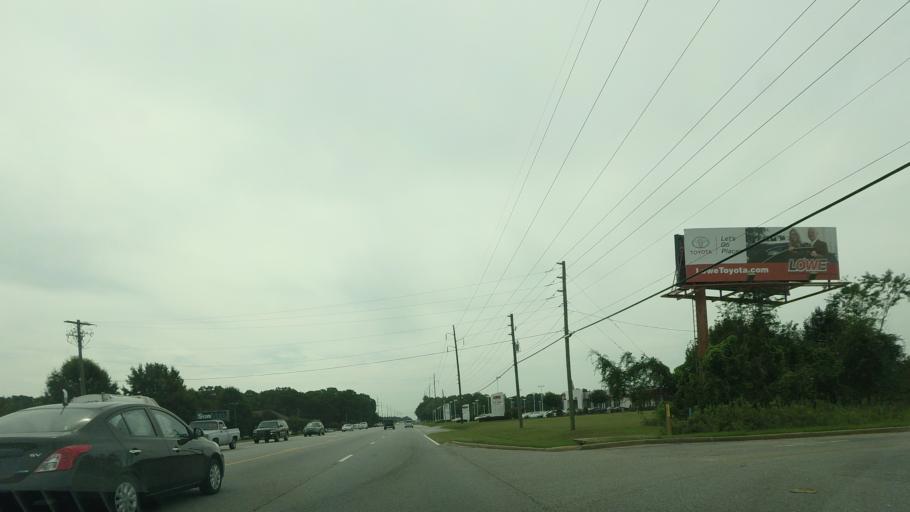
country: US
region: Georgia
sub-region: Houston County
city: Centerville
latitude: 32.6114
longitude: -83.6790
